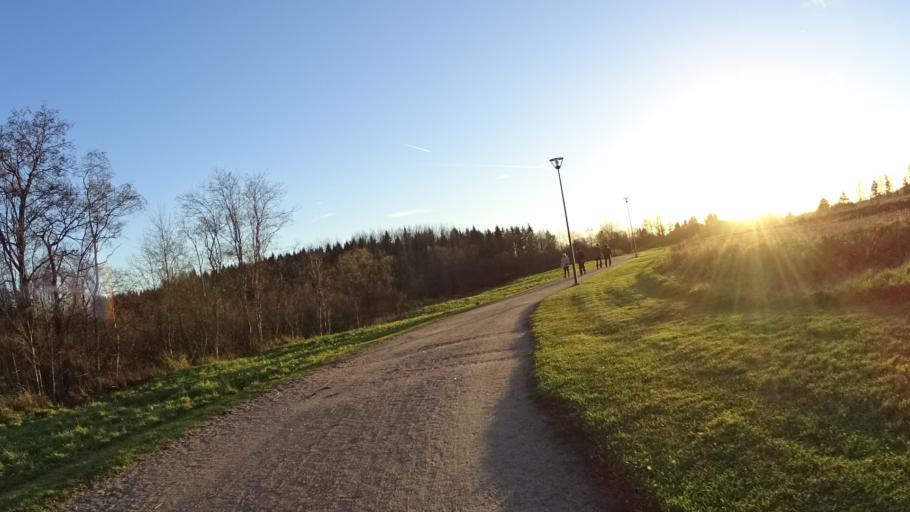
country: FI
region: Uusimaa
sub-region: Helsinki
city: Vantaa
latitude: 60.2828
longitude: 24.9969
